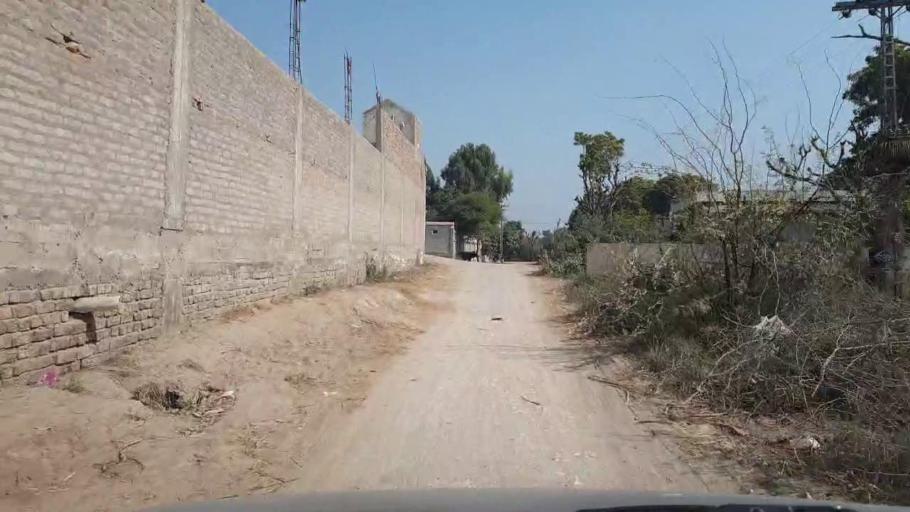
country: PK
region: Sindh
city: Tando Allahyar
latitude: 25.4270
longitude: 68.6531
